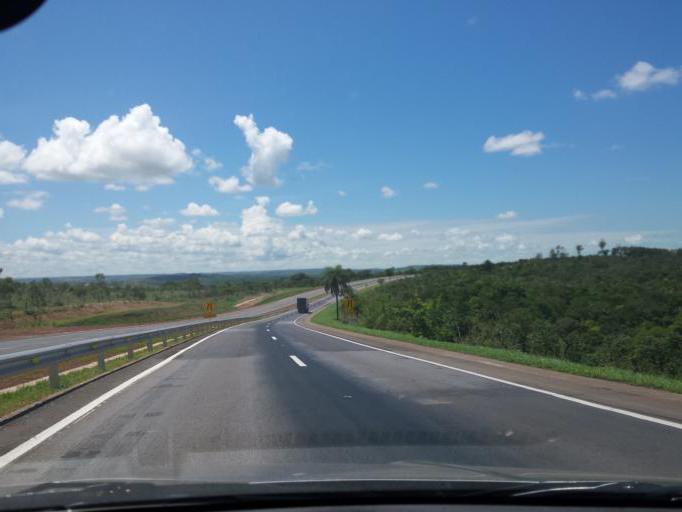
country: BR
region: Goias
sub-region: Luziania
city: Luziania
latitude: -16.5059
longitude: -47.8092
